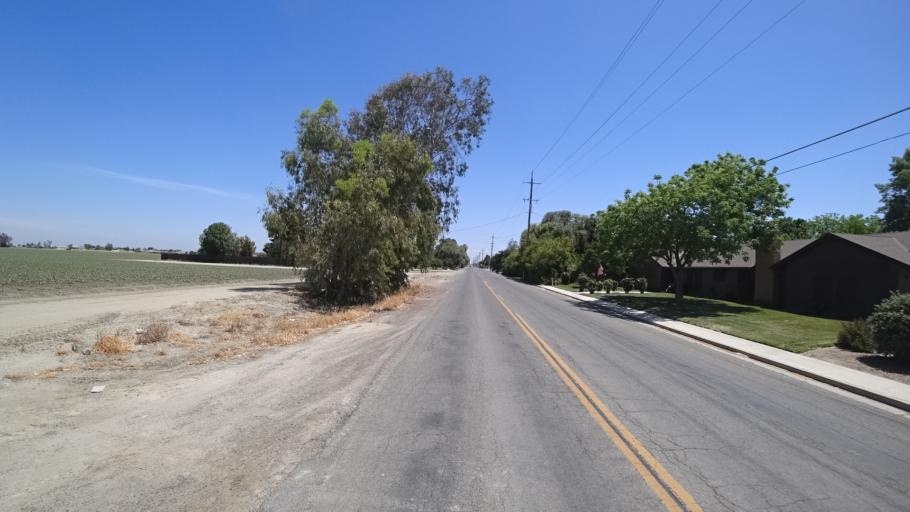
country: US
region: California
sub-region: Kings County
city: Corcoran
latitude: 36.1090
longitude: -119.5787
